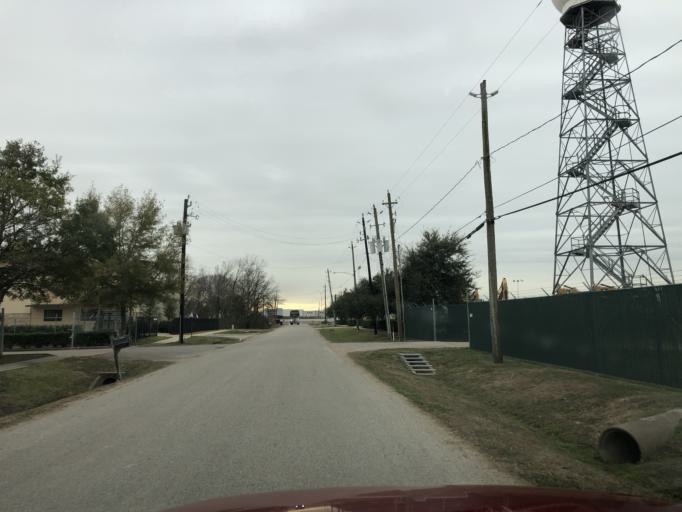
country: US
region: Texas
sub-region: Fort Bend County
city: Missouri City
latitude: 29.6353
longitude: -95.5252
